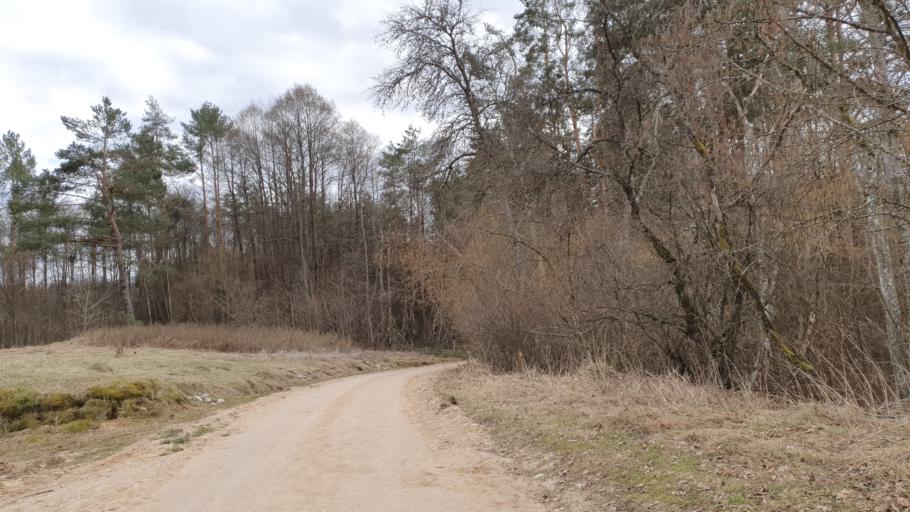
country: LT
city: Grigiskes
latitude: 54.7331
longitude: 25.0279
